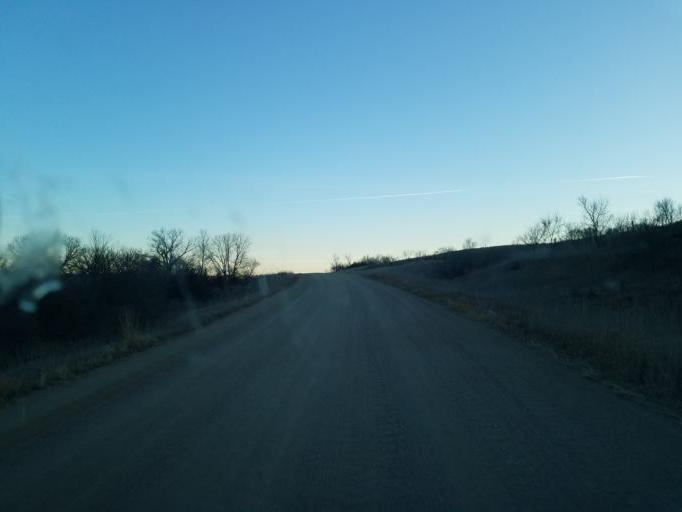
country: US
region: Nebraska
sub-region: Knox County
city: Center
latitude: 42.7005
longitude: -97.8985
